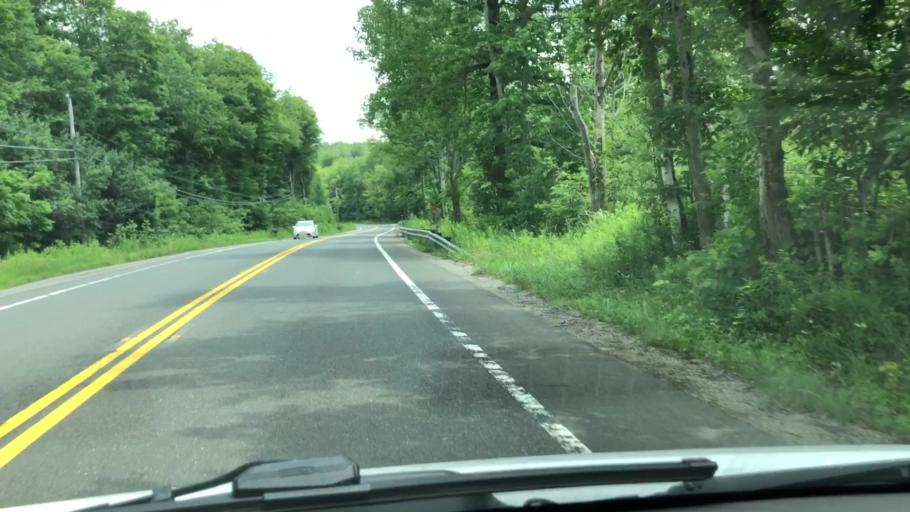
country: US
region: Massachusetts
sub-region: Berkshire County
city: Adams
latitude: 42.5815
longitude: -73.0742
